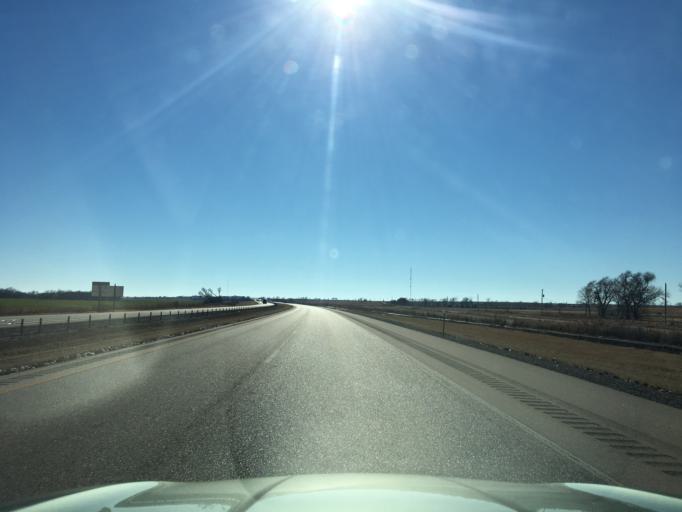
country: US
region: Oklahoma
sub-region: Kay County
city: Blackwell
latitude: 36.8971
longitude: -97.3543
